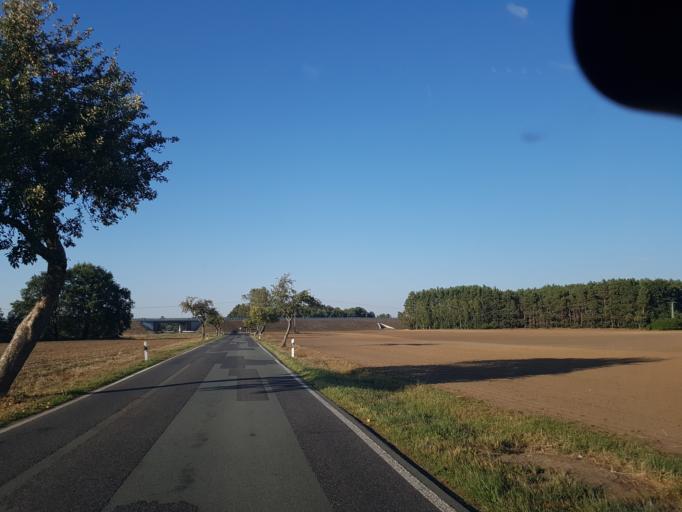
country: DE
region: Brandenburg
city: Bad Liebenwerda
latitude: 51.5018
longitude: 13.4049
